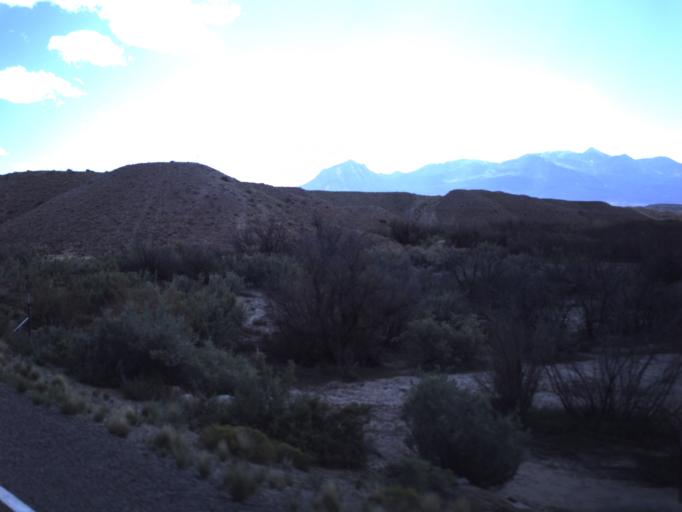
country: US
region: Utah
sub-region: Emery County
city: Ferron
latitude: 38.3252
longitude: -110.6771
